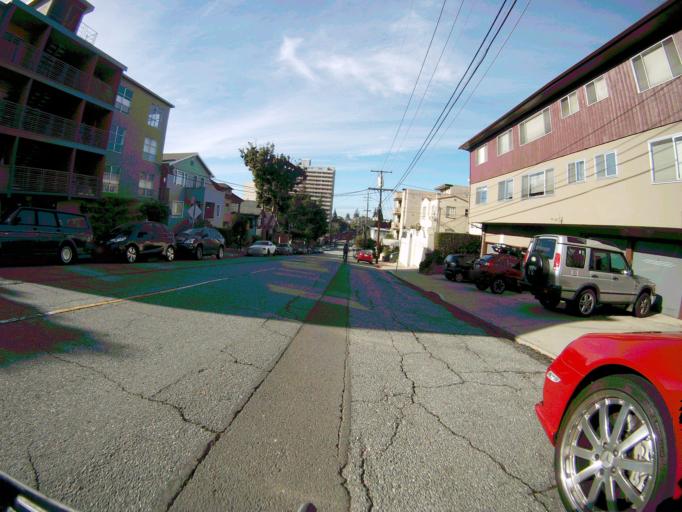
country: US
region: California
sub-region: Alameda County
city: Piedmont
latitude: 37.8254
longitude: -122.2483
